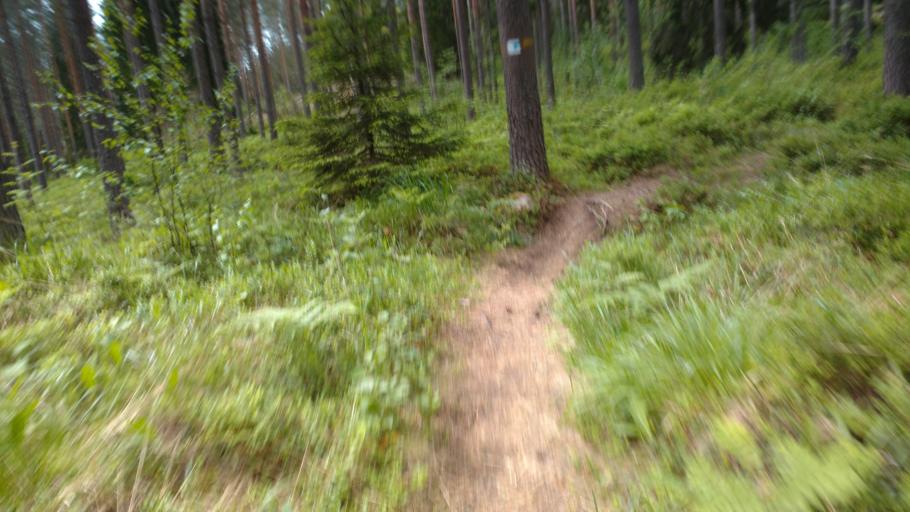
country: FI
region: Uusimaa
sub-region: Raaseporin
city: Pohja
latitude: 60.1182
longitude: 23.5568
